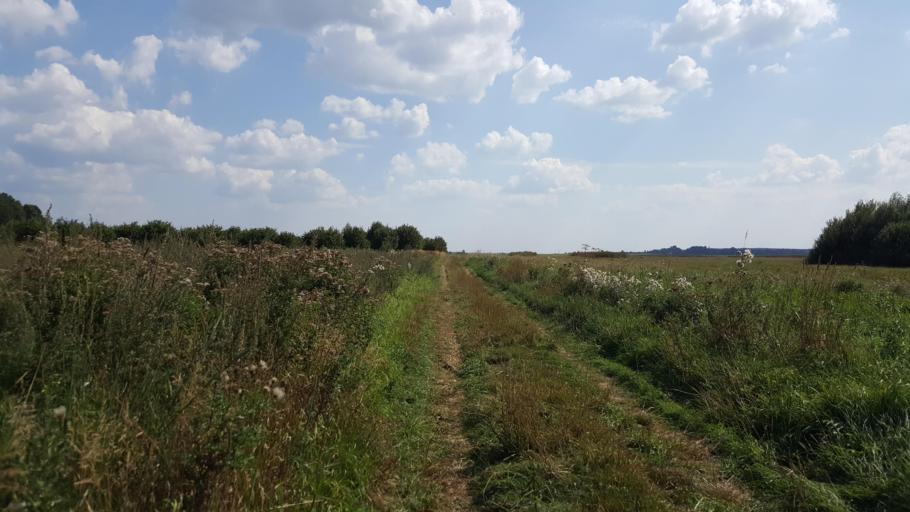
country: BY
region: Brest
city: Kamyanyuki
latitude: 52.4887
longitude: 23.6810
